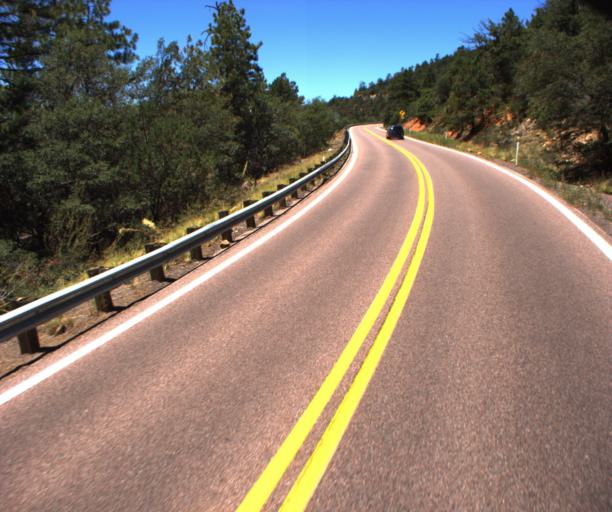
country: US
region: Arizona
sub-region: Gila County
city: Pine
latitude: 34.4170
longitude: -111.4984
